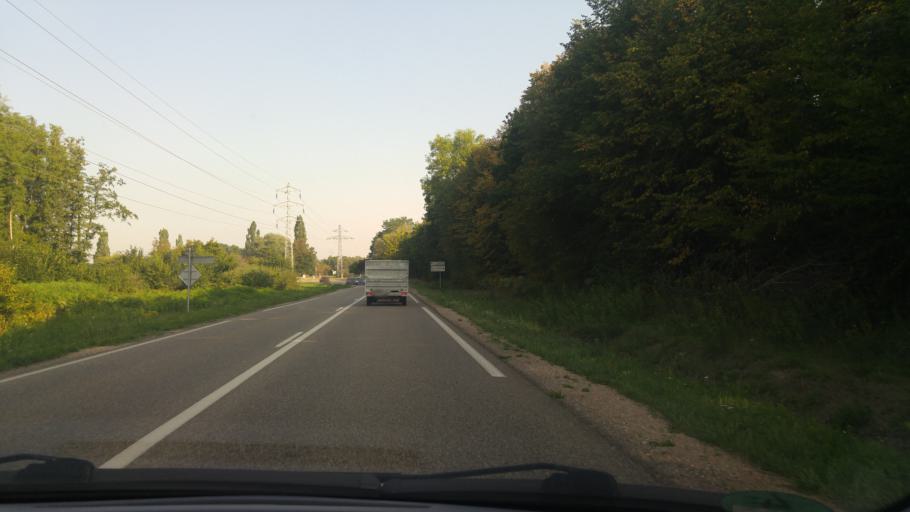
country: FR
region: Alsace
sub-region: Departement du Bas-Rhin
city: Durrenbach
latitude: 48.8770
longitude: 7.7604
